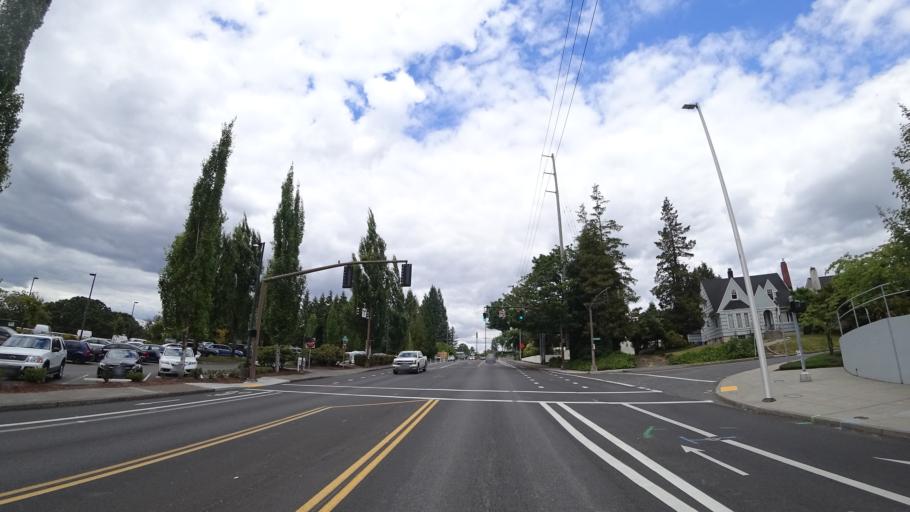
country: US
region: Oregon
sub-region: Multnomah County
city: Portland
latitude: 45.5603
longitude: -122.6947
